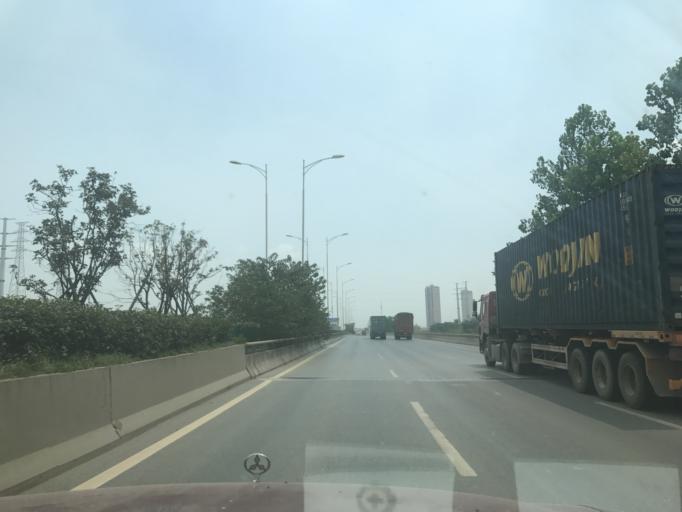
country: CN
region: Hubei
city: Houhu
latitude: 30.6700
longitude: 114.3011
